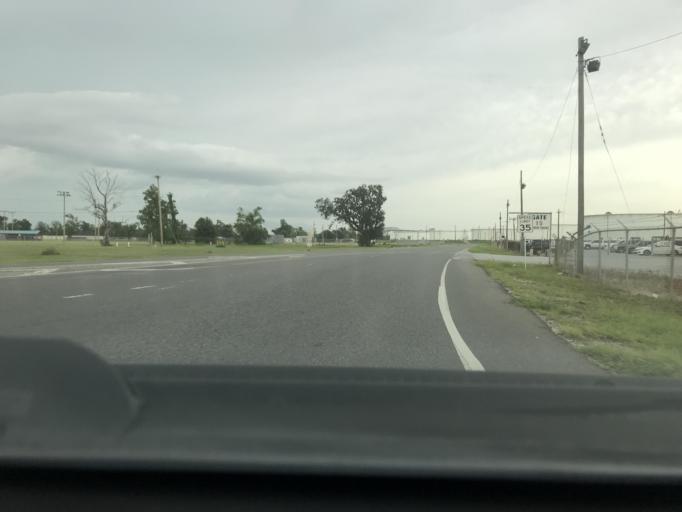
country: US
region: Louisiana
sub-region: Calcasieu Parish
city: Westlake
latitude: 30.2442
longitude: -93.2666
